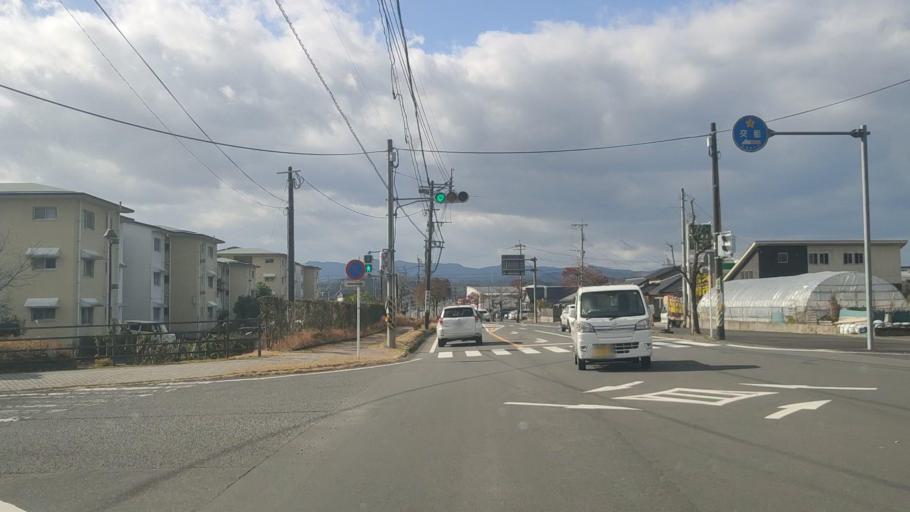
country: JP
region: Kagoshima
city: Okuchi-shinohara
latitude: 31.9540
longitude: 130.7217
